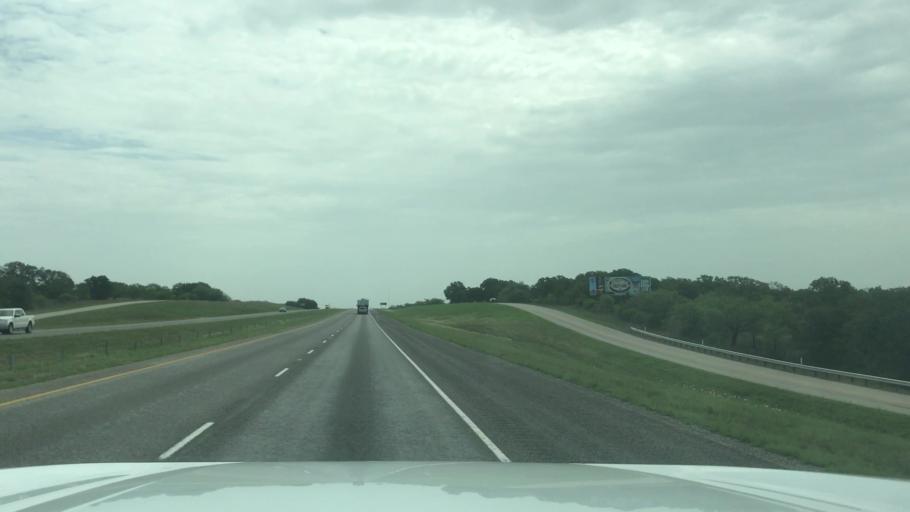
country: US
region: Texas
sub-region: Eastland County
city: Cisco
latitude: 32.3754
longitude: -98.9098
